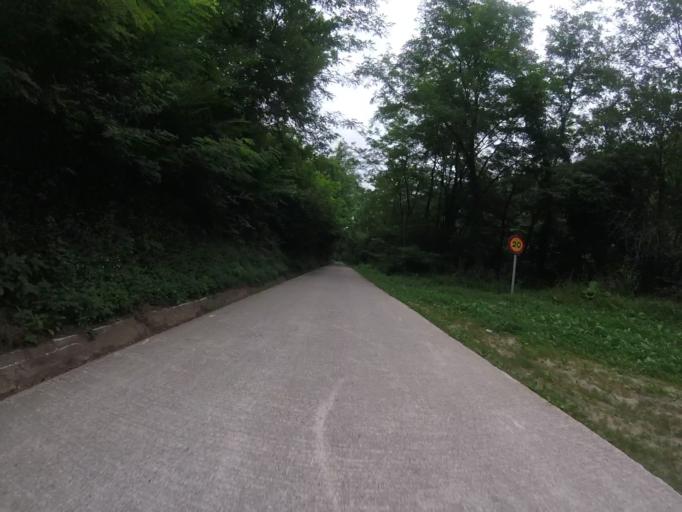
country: ES
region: Navarre
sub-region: Provincia de Navarra
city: Doneztebe
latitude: 43.1366
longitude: -1.6656
